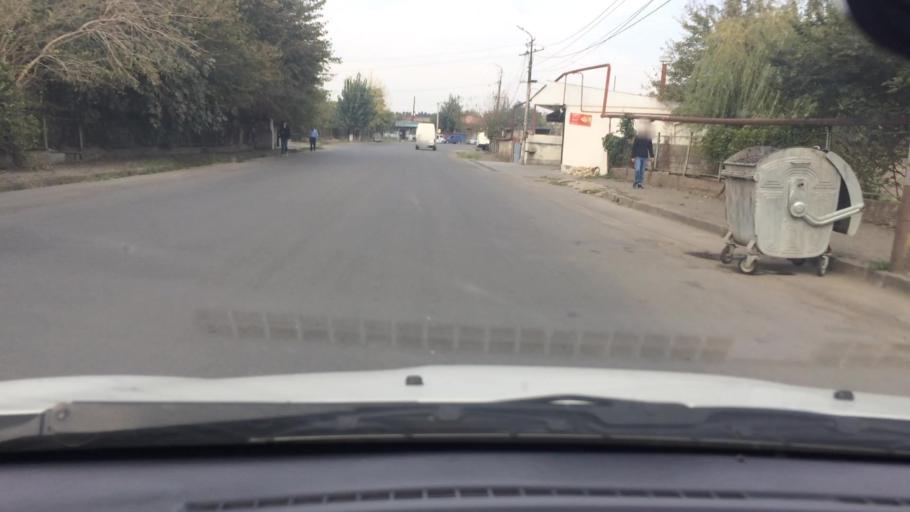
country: GE
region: Kvemo Kartli
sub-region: Marneuli
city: Marneuli
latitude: 41.4622
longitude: 44.8113
